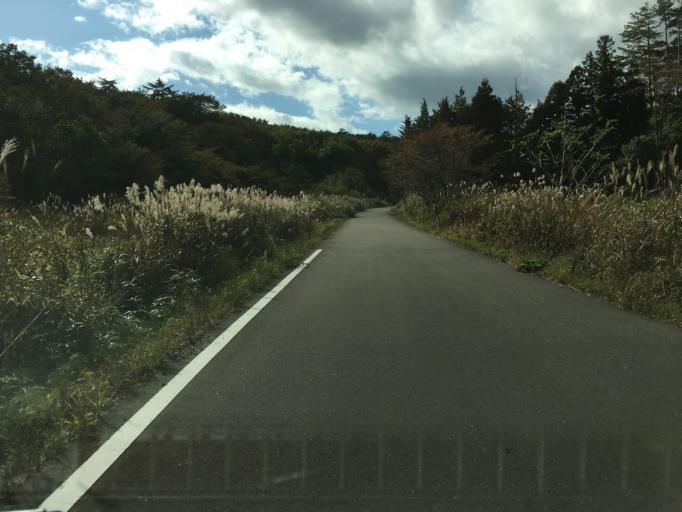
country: JP
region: Miyagi
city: Marumori
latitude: 37.8033
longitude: 140.7566
